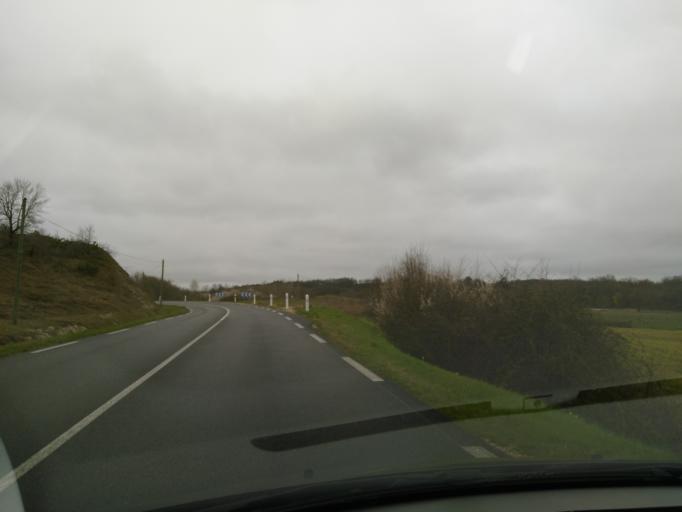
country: FR
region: Aquitaine
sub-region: Departement du Lot-et-Garonne
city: Castillonnes
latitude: 44.7214
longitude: 0.5572
